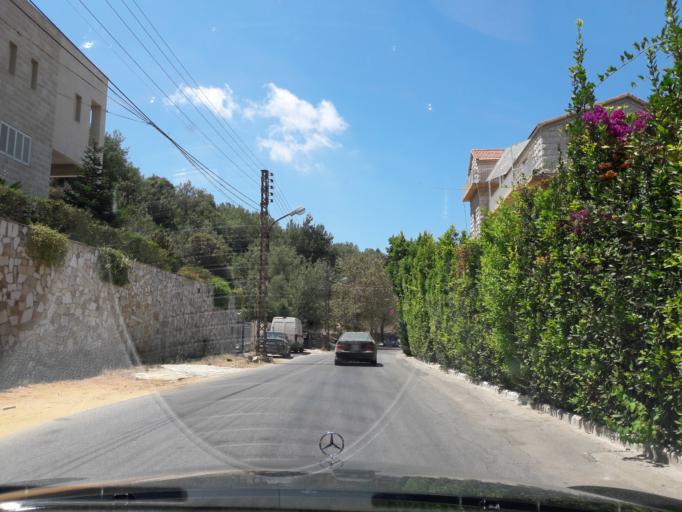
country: LB
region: Mont-Liban
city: Djounie
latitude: 33.9255
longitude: 35.6669
